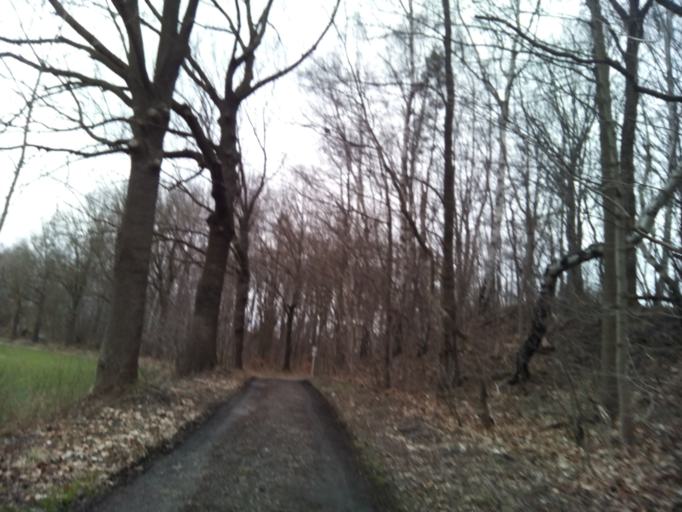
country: DE
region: Saxony
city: Brand-Erbisdorf
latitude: 50.8820
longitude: 13.3305
